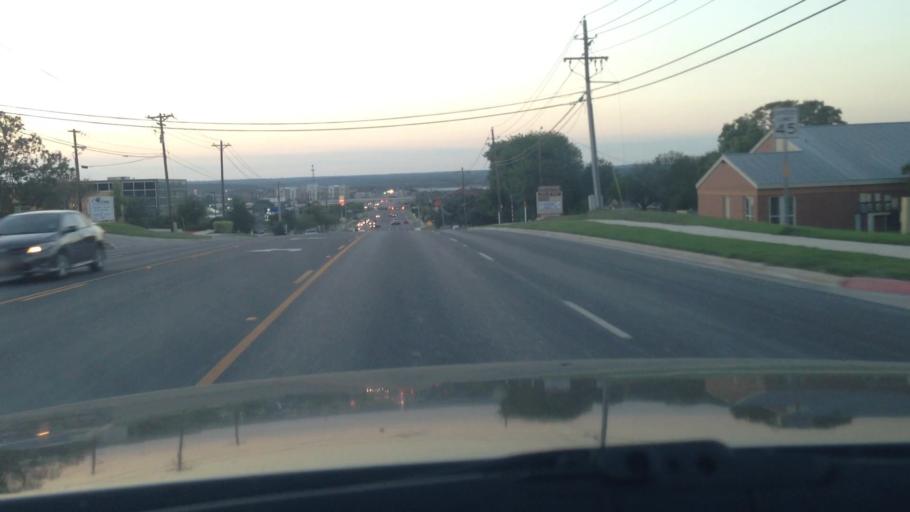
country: US
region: Texas
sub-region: Hays County
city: San Marcos
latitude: 29.8524
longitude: -97.9477
